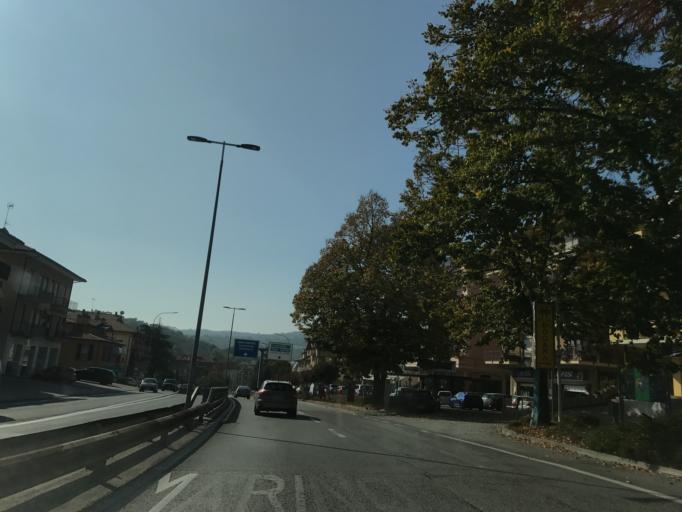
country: SM
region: Serravalle
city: Serravalle
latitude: 43.9798
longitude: 12.4891
